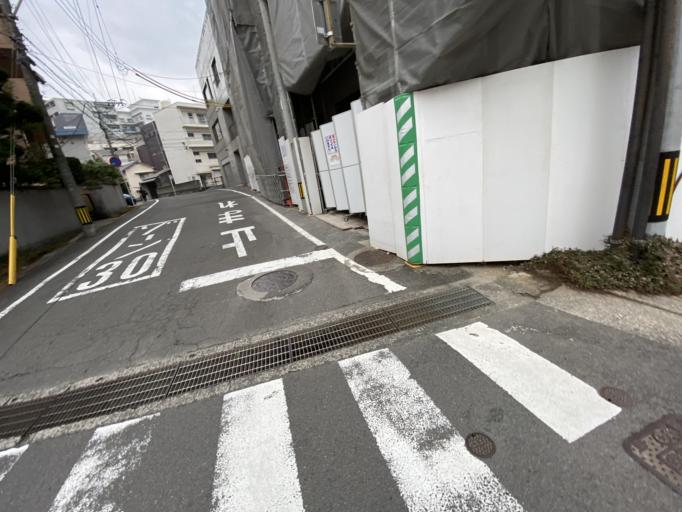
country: JP
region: Nagasaki
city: Nagasaki-shi
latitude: 32.7490
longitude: 129.8742
